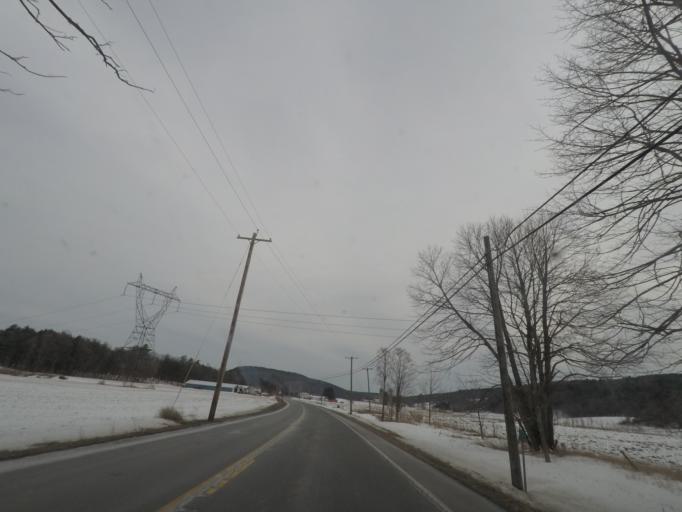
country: US
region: New York
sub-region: Albany County
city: Voorheesville
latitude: 42.5816
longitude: -73.9807
